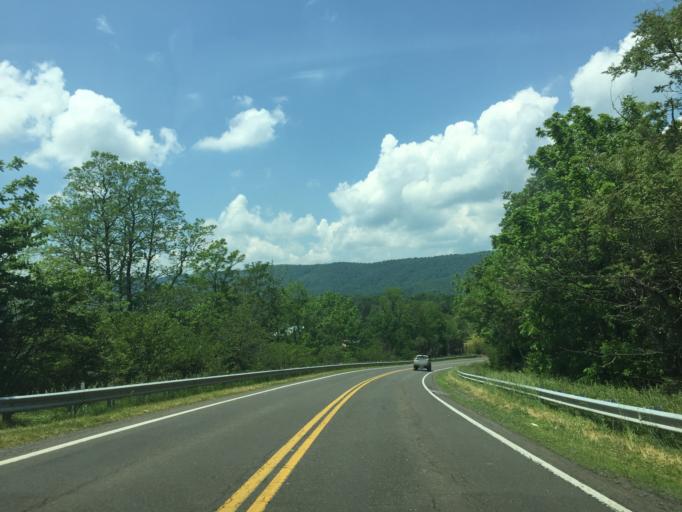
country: US
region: Virginia
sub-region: Shenandoah County
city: Strasburg
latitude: 39.0338
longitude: -78.3798
